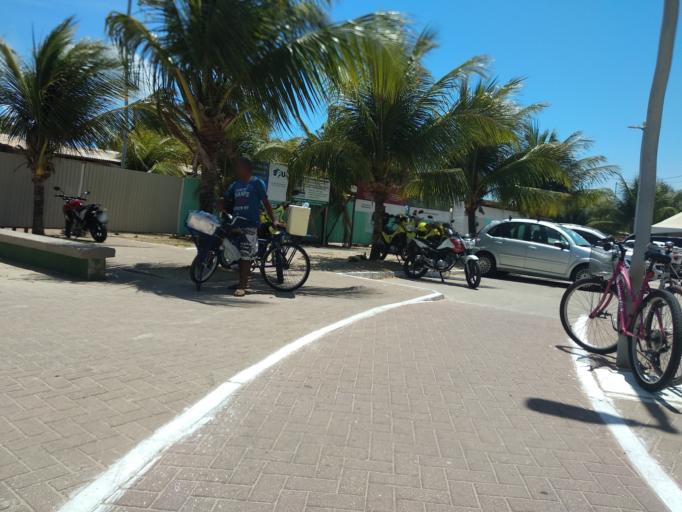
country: BR
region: Alagoas
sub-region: Maceio
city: Maceio
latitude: -9.6646
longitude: -35.6960
